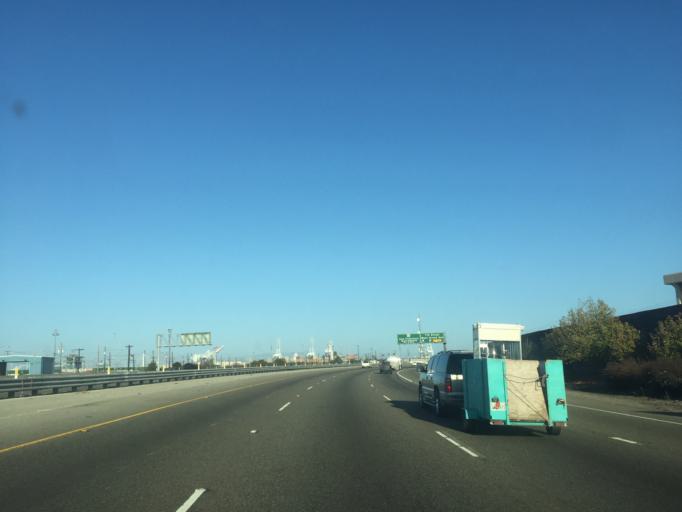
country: US
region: California
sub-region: Alameda County
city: Oakland
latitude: 37.8031
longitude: -122.3005
